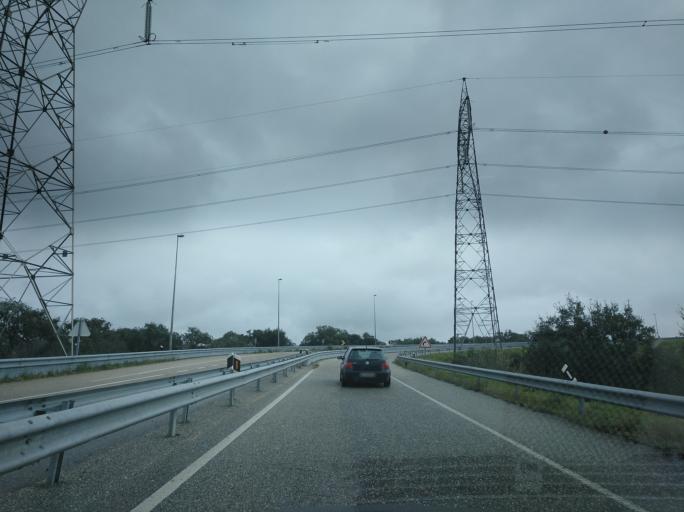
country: PT
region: Setubal
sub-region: Grandola
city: Grandola
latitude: 38.1692
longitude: -8.5535
